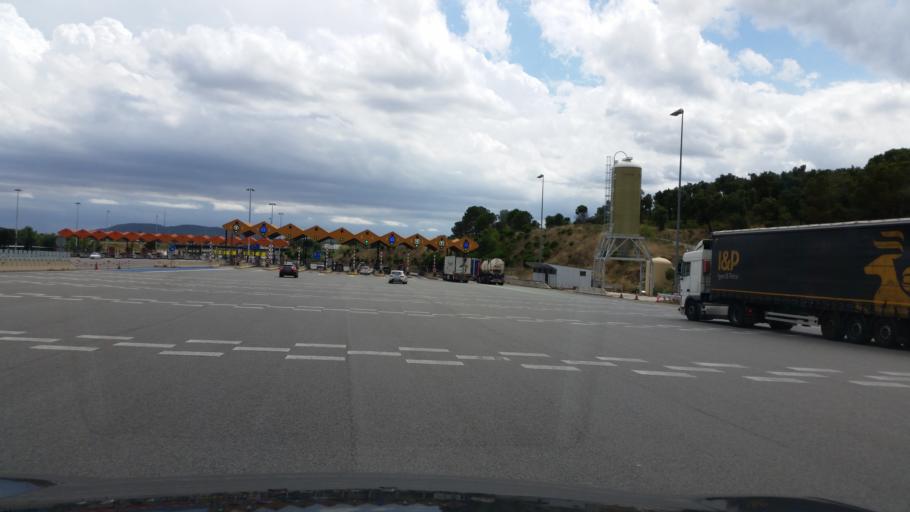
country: ES
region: Catalonia
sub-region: Provincia de Girona
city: la Jonquera
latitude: 42.4123
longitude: 2.8721
